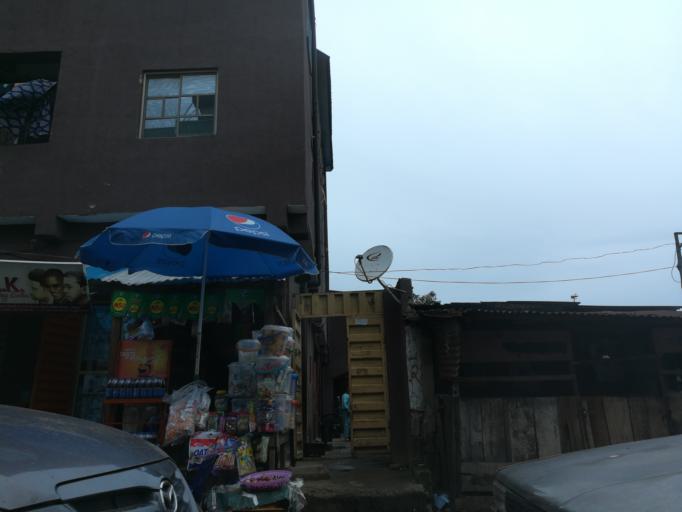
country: NG
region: Lagos
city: Ebute Metta
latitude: 6.4846
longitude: 3.3872
